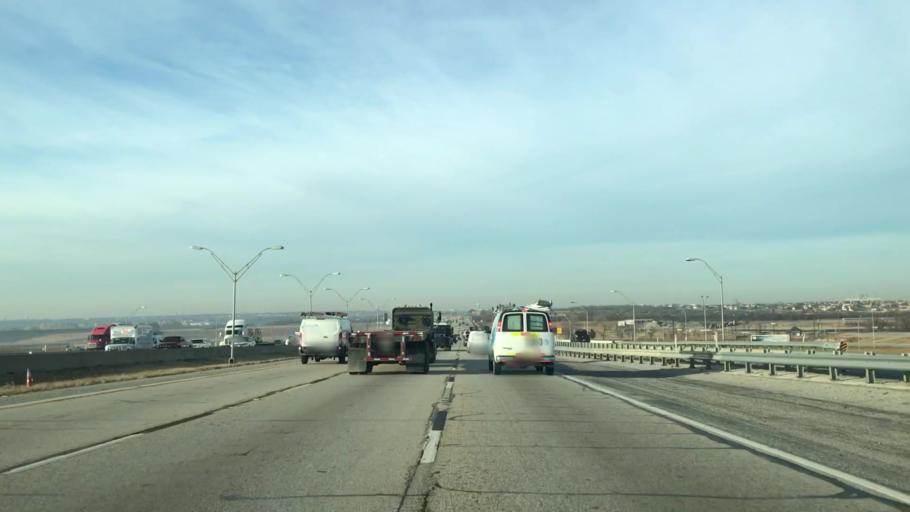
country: US
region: Texas
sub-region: Tarrant County
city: Saginaw
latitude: 32.8374
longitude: -97.3613
